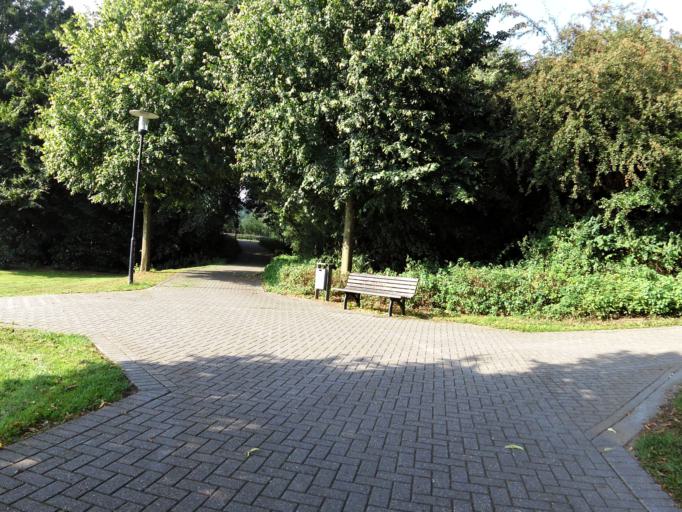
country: DE
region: North Rhine-Westphalia
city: Geilenkirchen
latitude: 50.9597
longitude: 6.1162
